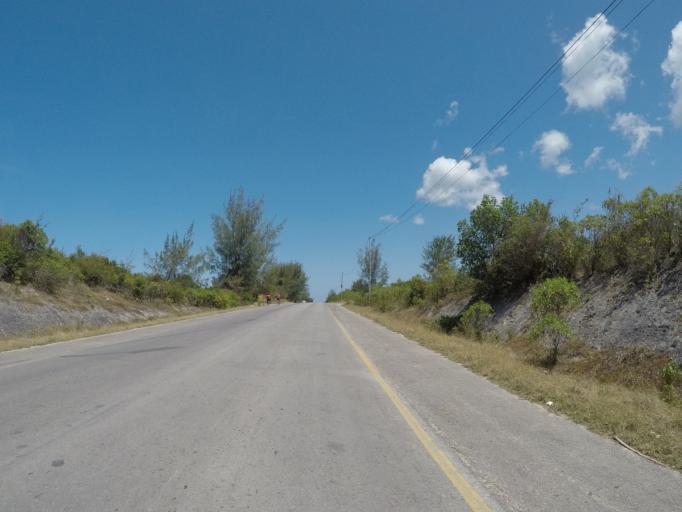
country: TZ
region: Zanzibar Central/South
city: Nganane
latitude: -6.2845
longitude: 39.5361
